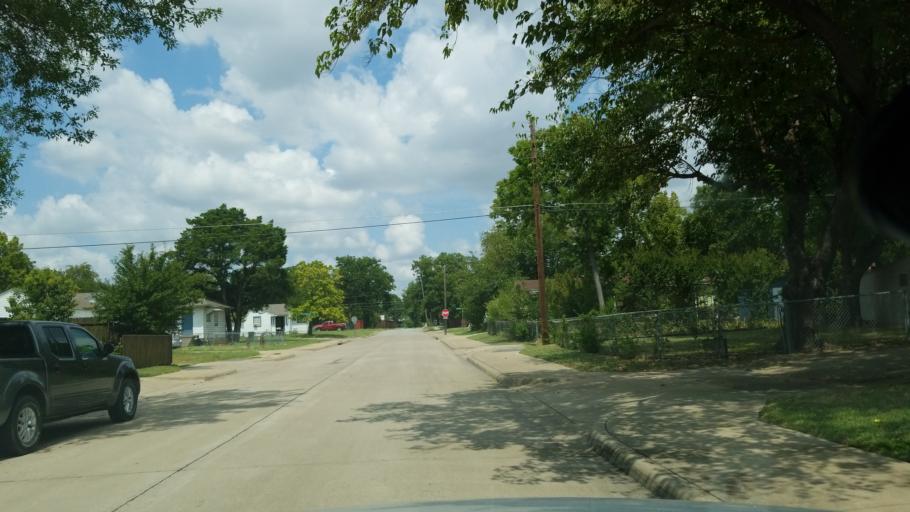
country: US
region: Texas
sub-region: Dallas County
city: Garland
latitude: 32.9191
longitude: -96.6520
